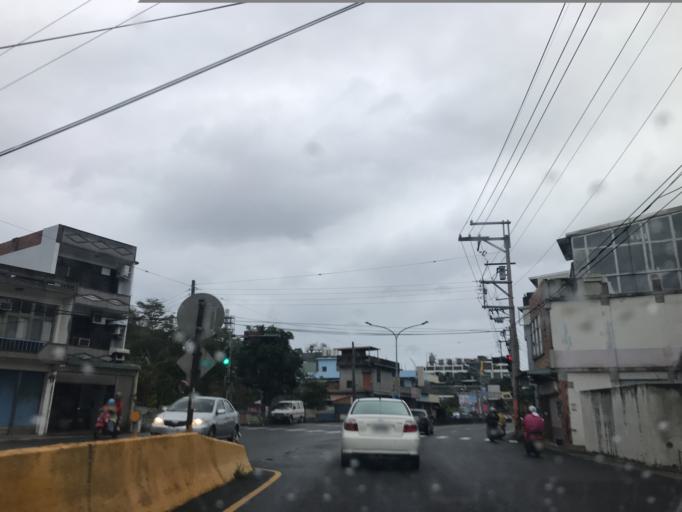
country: TW
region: Taiwan
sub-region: Hsinchu
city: Zhubei
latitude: 24.8246
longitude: 121.0619
